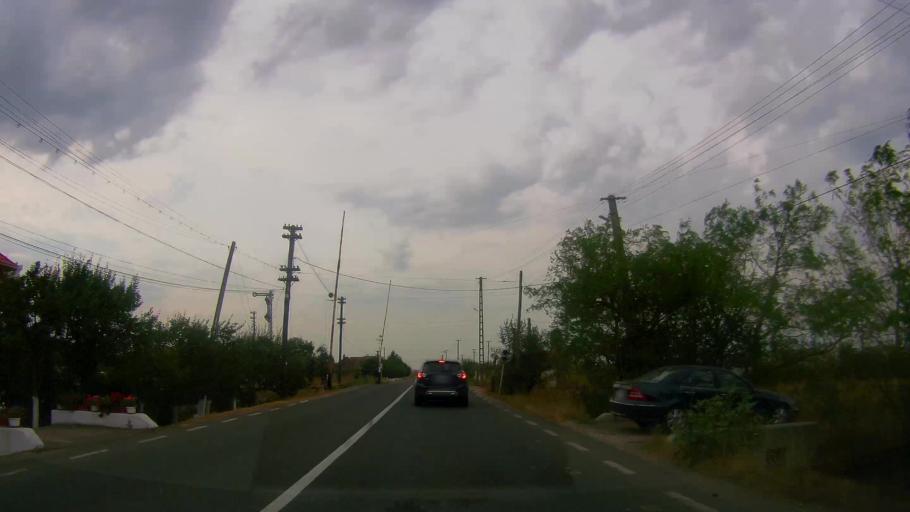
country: RO
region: Satu Mare
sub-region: Comuna Acas
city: Acas
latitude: 47.5262
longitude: 22.7822
